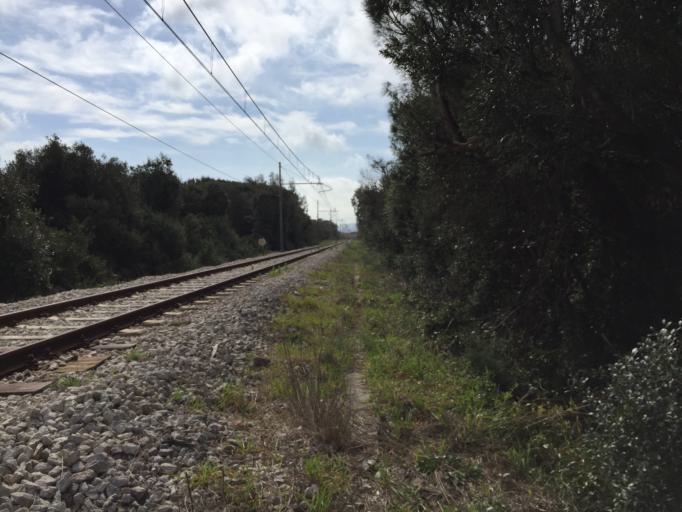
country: IT
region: Campania
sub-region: Provincia di Napoli
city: Monterusciello
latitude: 40.8459
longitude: 14.0494
